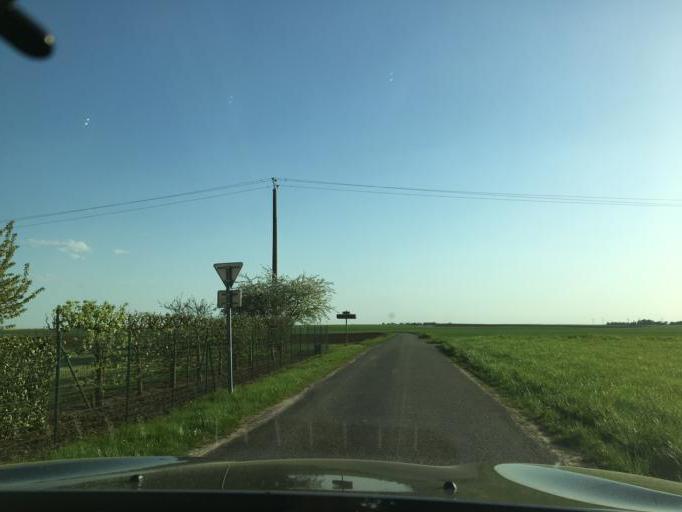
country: FR
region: Centre
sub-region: Departement du Loiret
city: Epieds-en-Beauce
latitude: 47.9260
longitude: 1.5824
